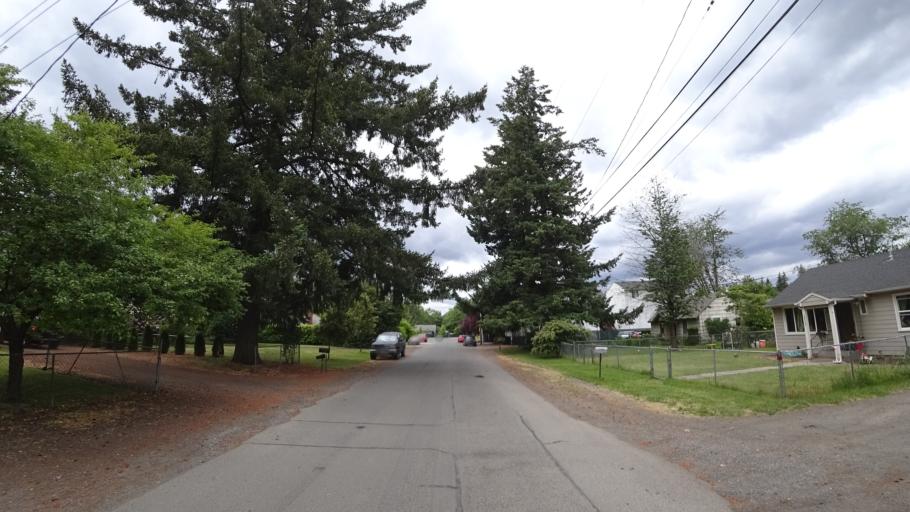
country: US
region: Oregon
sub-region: Multnomah County
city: Lents
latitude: 45.4847
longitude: -122.5360
